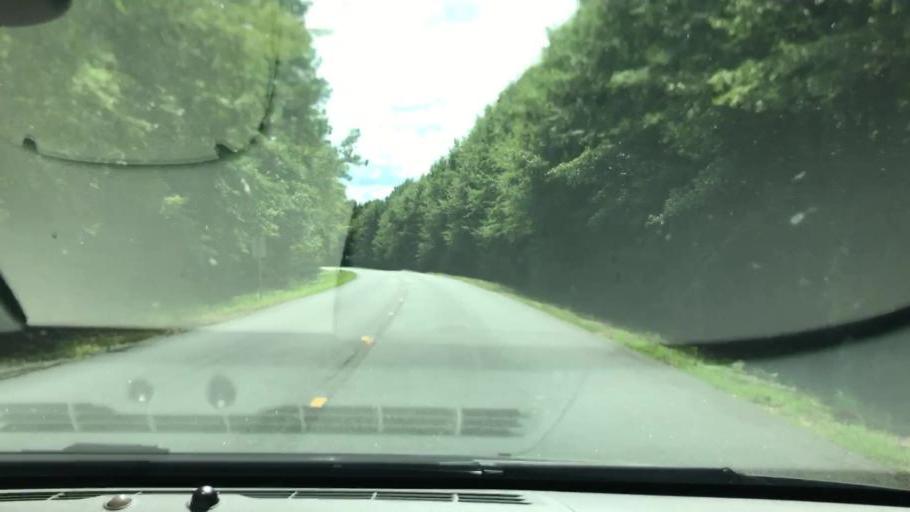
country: US
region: Georgia
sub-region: Quitman County
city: Georgetown
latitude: 31.9864
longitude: -85.0492
